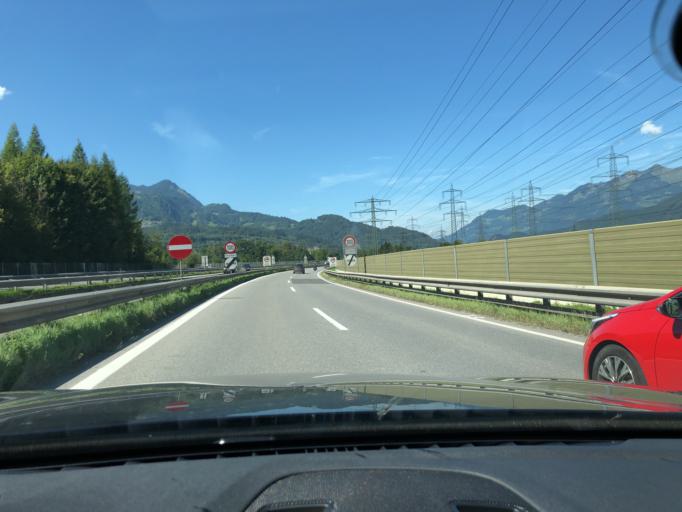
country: AT
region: Vorarlberg
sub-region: Politischer Bezirk Bludenz
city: Bludenz
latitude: 47.1377
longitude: 9.8298
